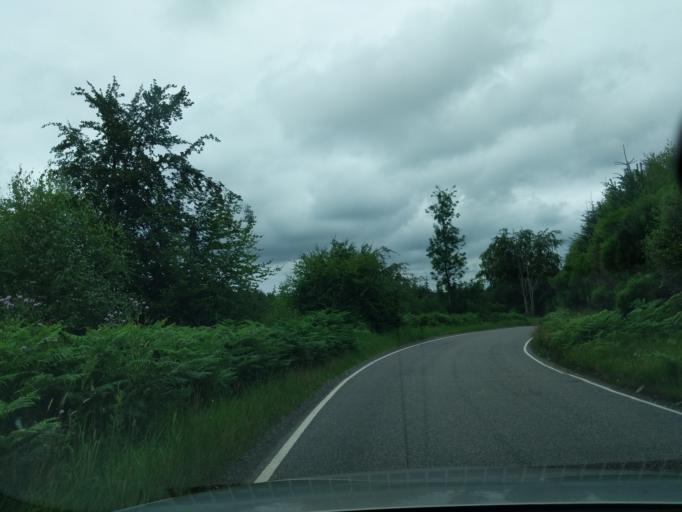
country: GB
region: Scotland
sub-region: Moray
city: Forres
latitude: 57.5203
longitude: -3.6776
